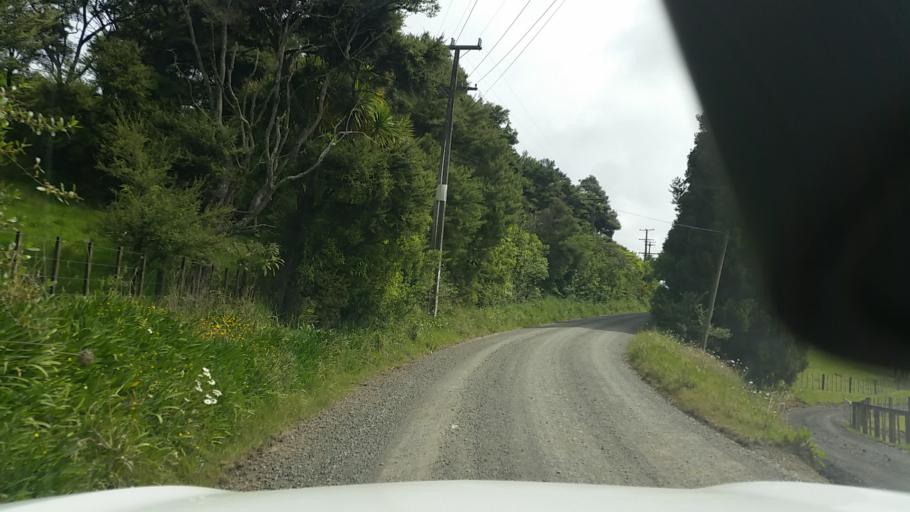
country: NZ
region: Auckland
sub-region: Auckland
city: Muriwai Beach
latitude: -36.8496
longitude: 174.5231
